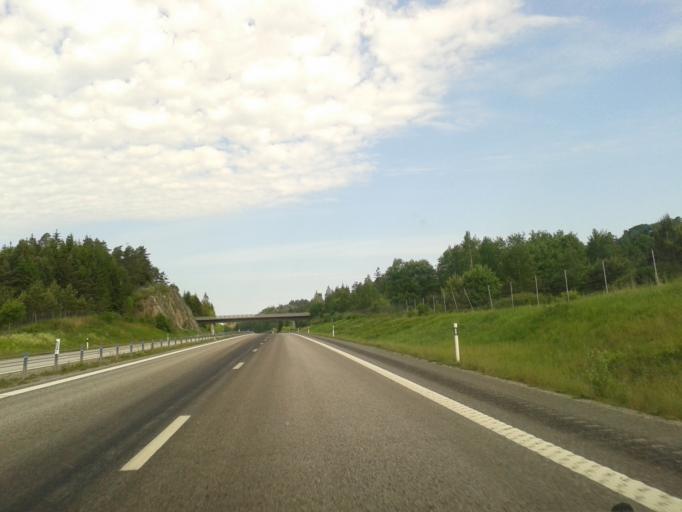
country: SE
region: Vaestra Goetaland
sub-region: Lysekils Kommun
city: Brastad
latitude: 58.5476
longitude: 11.5128
